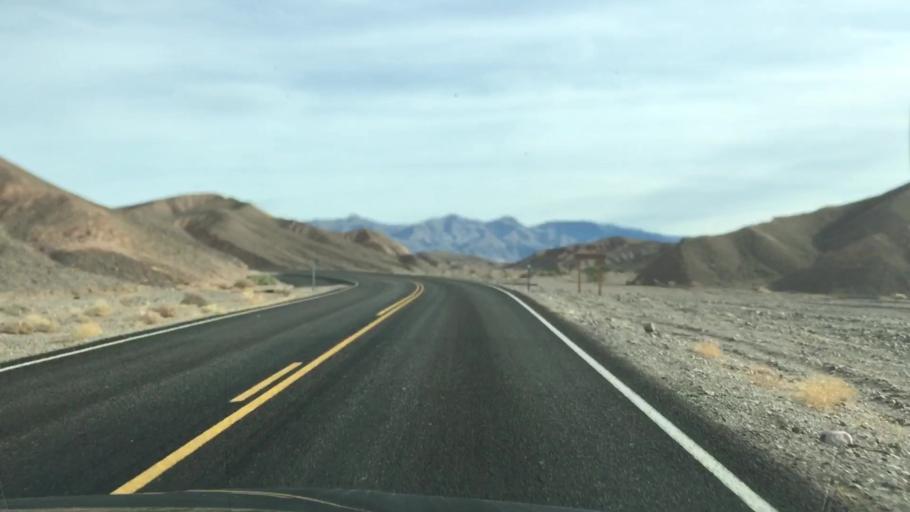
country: US
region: Nevada
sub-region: Nye County
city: Beatty
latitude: 36.6494
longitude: -117.0326
